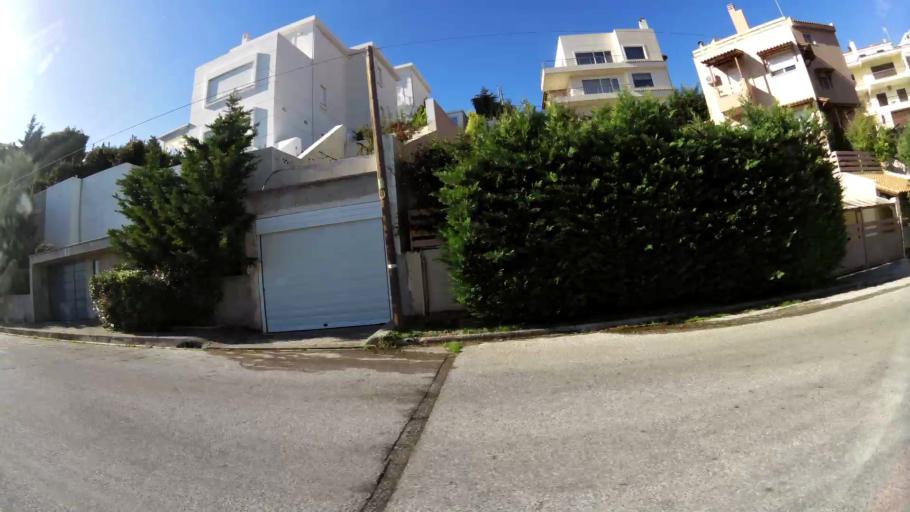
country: GR
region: Attica
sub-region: Nomarchia Anatolikis Attikis
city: Dhrafi
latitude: 38.0301
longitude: 23.8954
